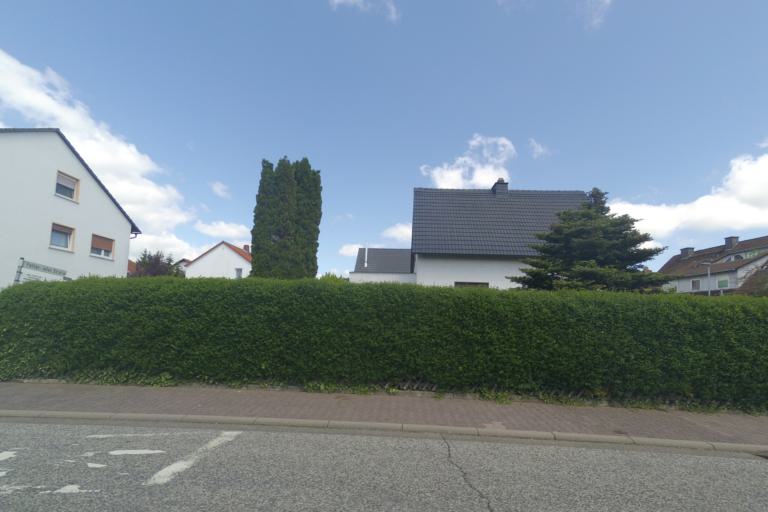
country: DE
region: Hesse
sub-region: Regierungsbezirk Darmstadt
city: Friedrichsdorf
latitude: 50.2545
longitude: 8.6783
